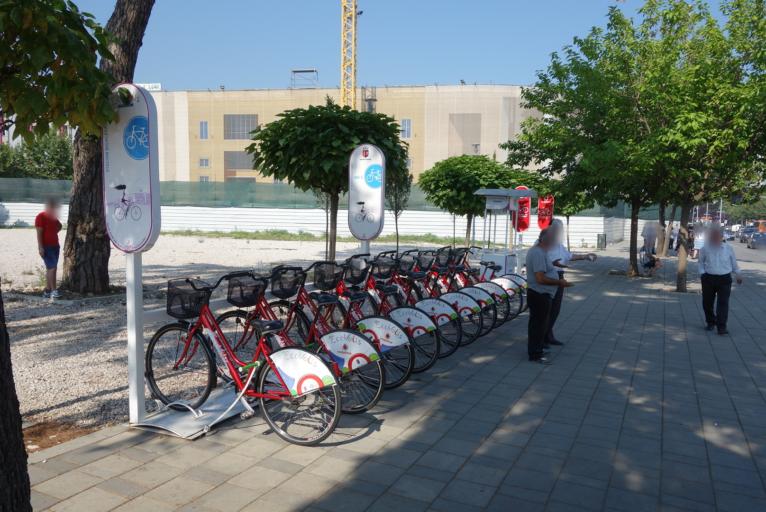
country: AL
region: Tirane
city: Tirana
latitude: 41.3280
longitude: 19.8178
